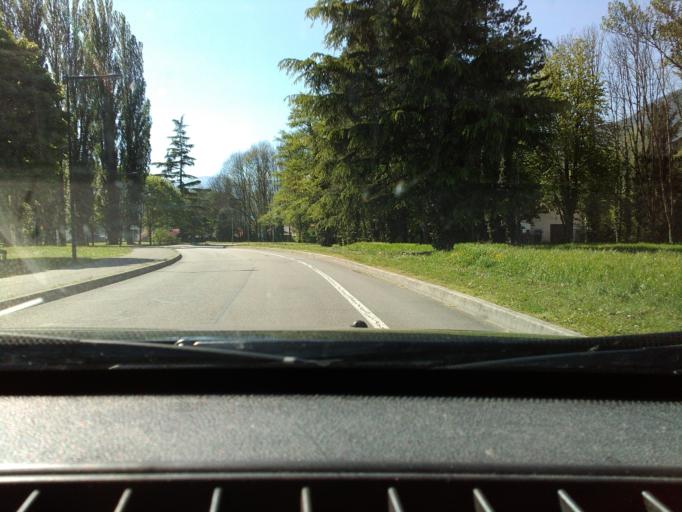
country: FR
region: Rhone-Alpes
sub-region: Departement de l'Isere
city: Corenc
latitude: 45.1947
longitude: 5.7646
